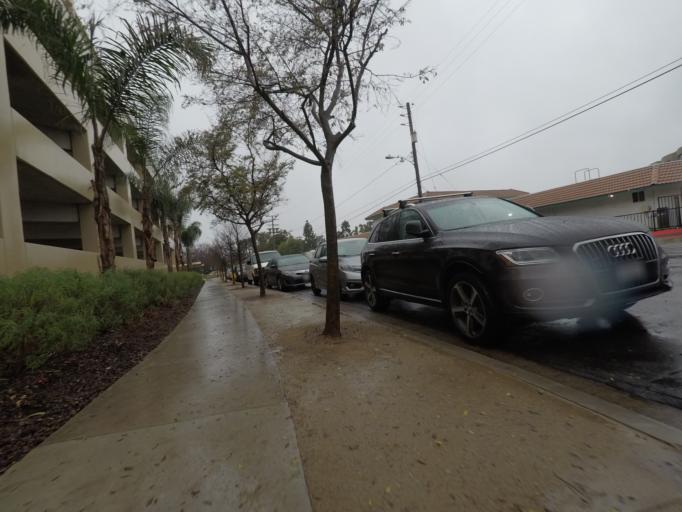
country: US
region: California
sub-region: San Diego County
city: San Diego
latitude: 32.7979
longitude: -117.1533
